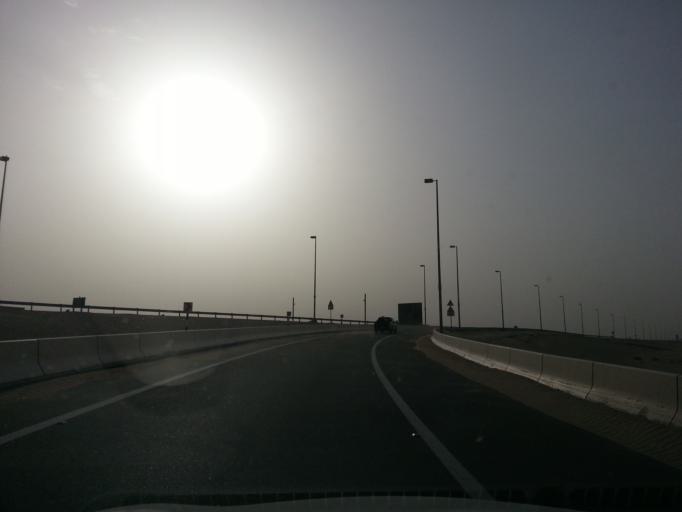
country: AE
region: Dubai
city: Dubai
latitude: 24.7936
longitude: 55.0770
